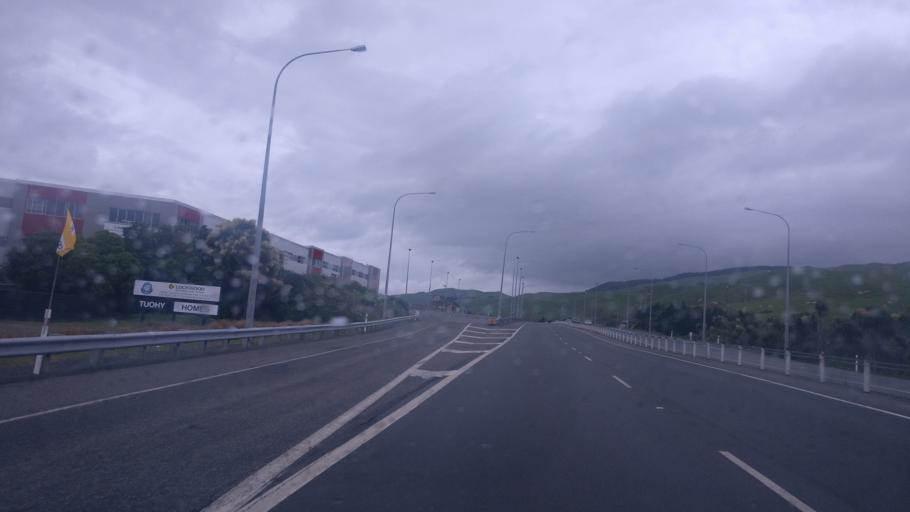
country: NZ
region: Wellington
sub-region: Porirua City
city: Porirua
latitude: -41.0789
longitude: 174.8721
